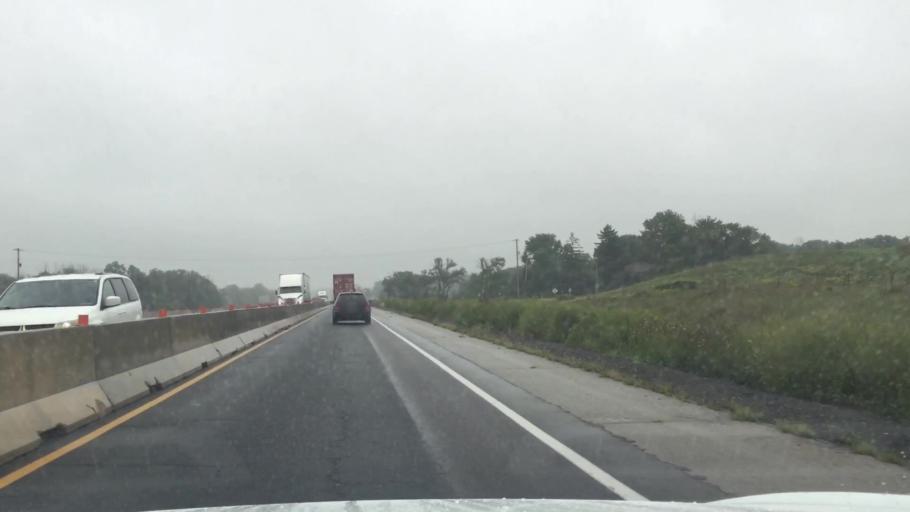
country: CA
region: Ontario
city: Delaware
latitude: 42.8157
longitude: -81.3164
